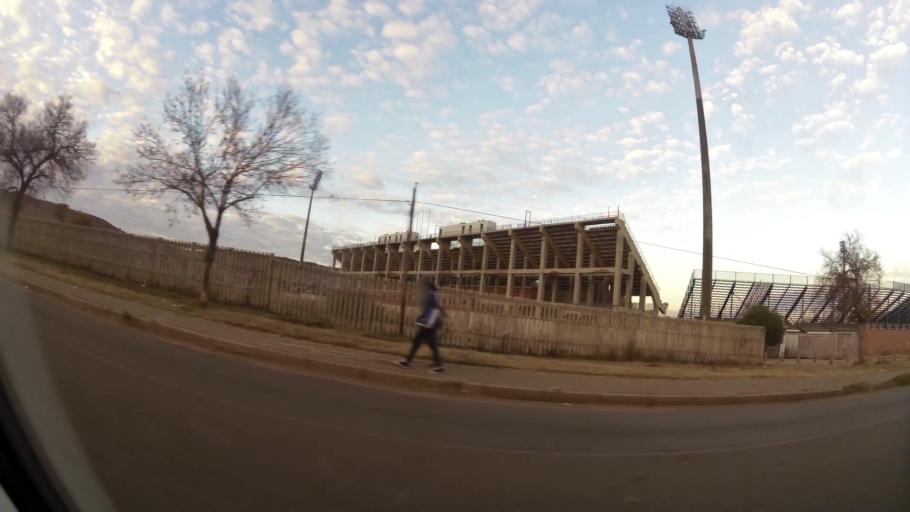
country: ZA
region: Gauteng
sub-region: City of Tshwane Metropolitan Municipality
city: Pretoria
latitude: -25.7077
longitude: 28.3373
